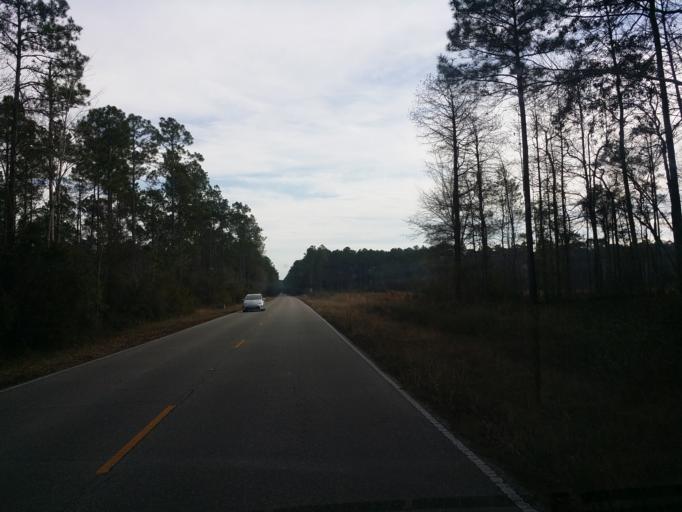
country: US
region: Florida
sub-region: Leon County
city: Woodville
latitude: 30.1631
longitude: -84.1549
